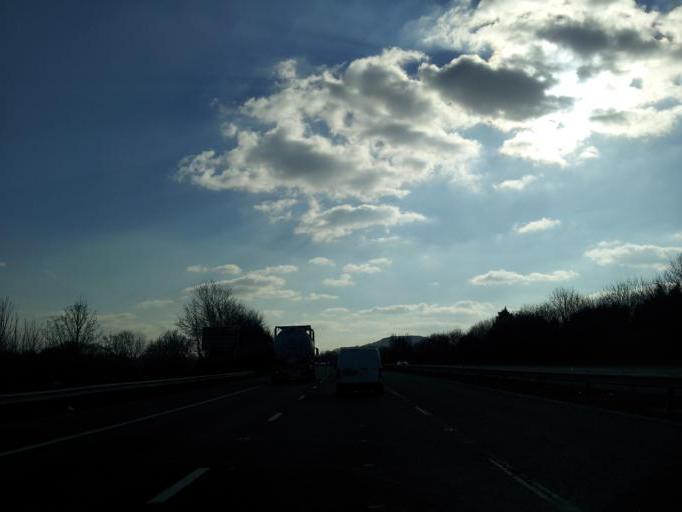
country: GB
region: England
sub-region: North Somerset
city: Bleadon
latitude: 51.2736
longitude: -2.9176
